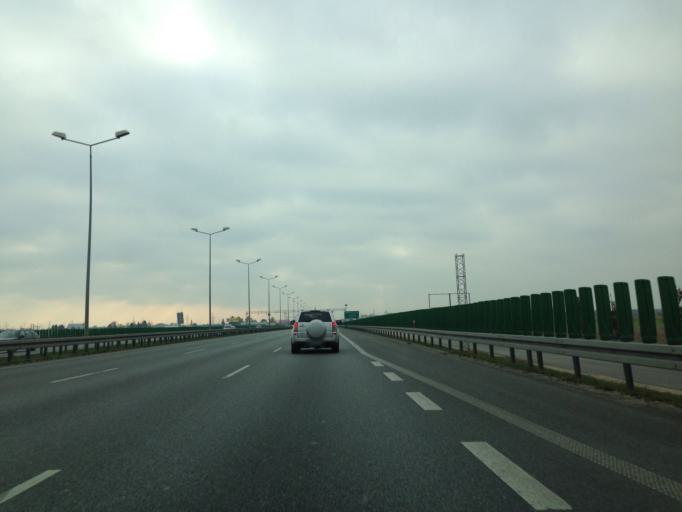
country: PL
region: Masovian Voivodeship
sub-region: Warszawa
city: Bemowo
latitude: 52.2360
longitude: 20.8844
